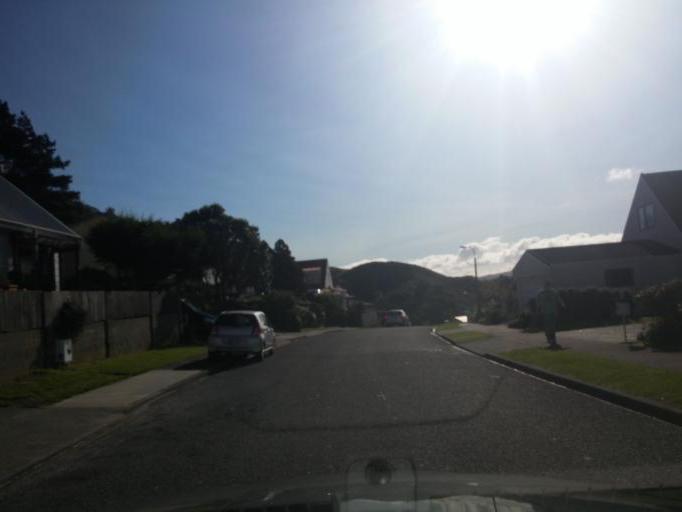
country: NZ
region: Wellington
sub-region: Wellington City
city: Wellington
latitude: -41.2322
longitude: 174.7919
